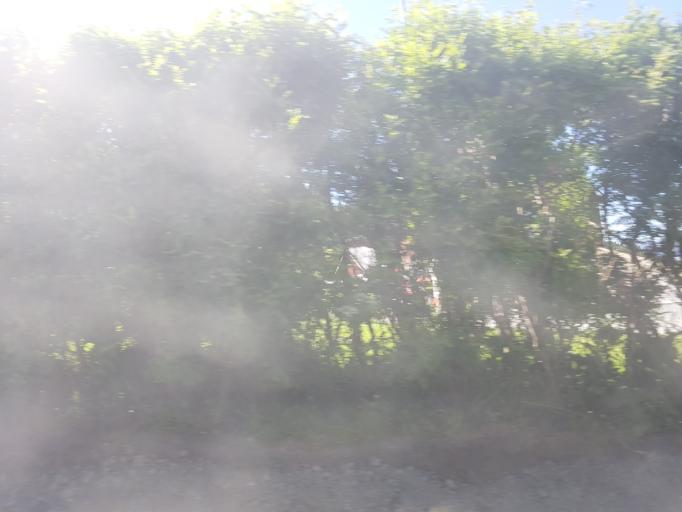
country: NO
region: Sor-Trondelag
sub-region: Skaun
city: Borsa
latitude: 63.4415
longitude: 10.1955
